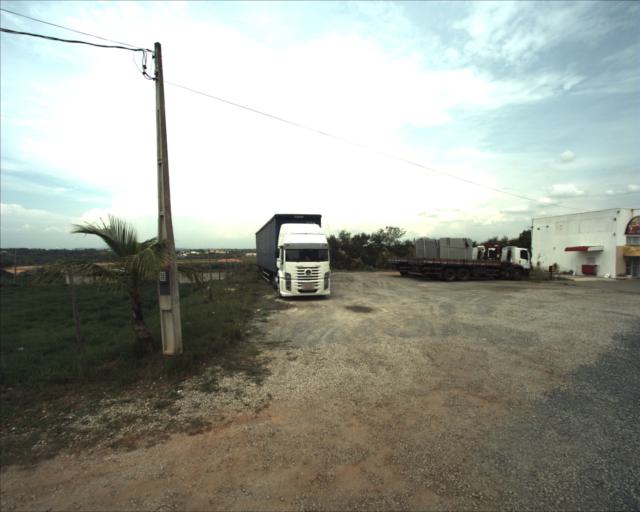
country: BR
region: Sao Paulo
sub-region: Sorocaba
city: Sorocaba
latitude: -23.4486
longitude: -47.4404
